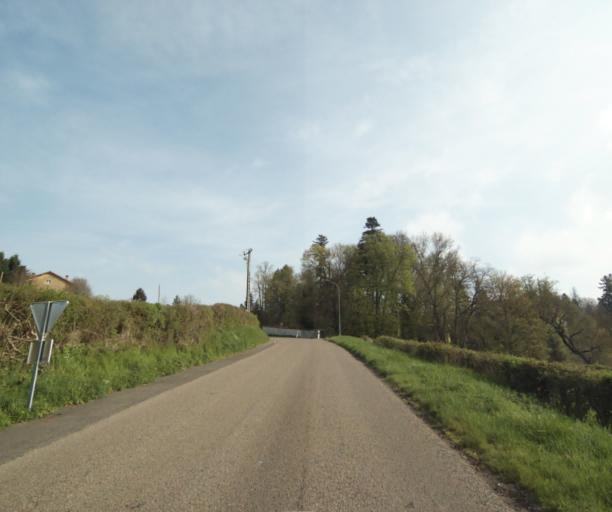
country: FR
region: Bourgogne
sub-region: Departement de Saone-et-Loire
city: Charolles
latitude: 46.4103
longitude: 4.2093
